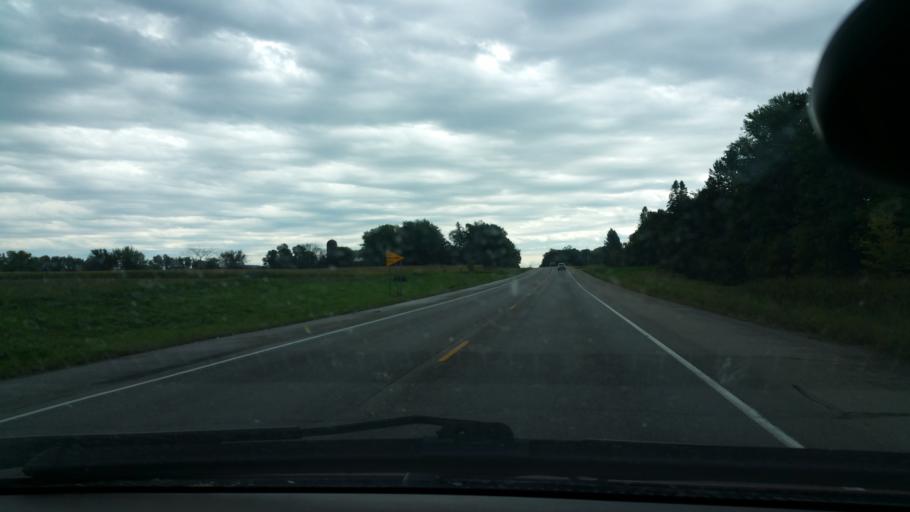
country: US
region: Minnesota
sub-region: Rice County
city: Dundas
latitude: 44.4719
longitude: -93.2770
